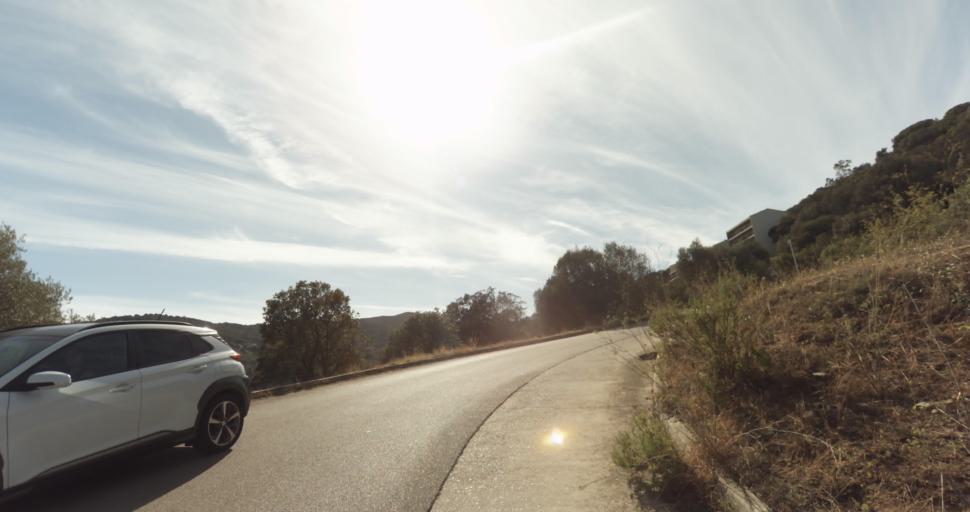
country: FR
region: Corsica
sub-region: Departement de la Corse-du-Sud
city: Ajaccio
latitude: 41.9344
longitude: 8.7192
